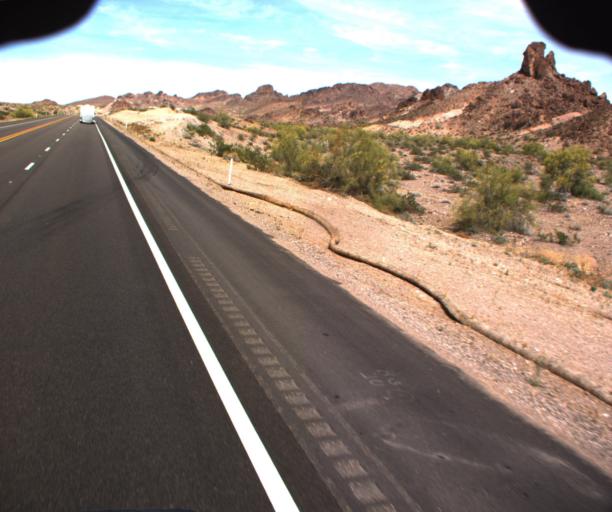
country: US
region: Arizona
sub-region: Mohave County
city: Desert Hills
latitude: 34.6173
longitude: -114.3449
